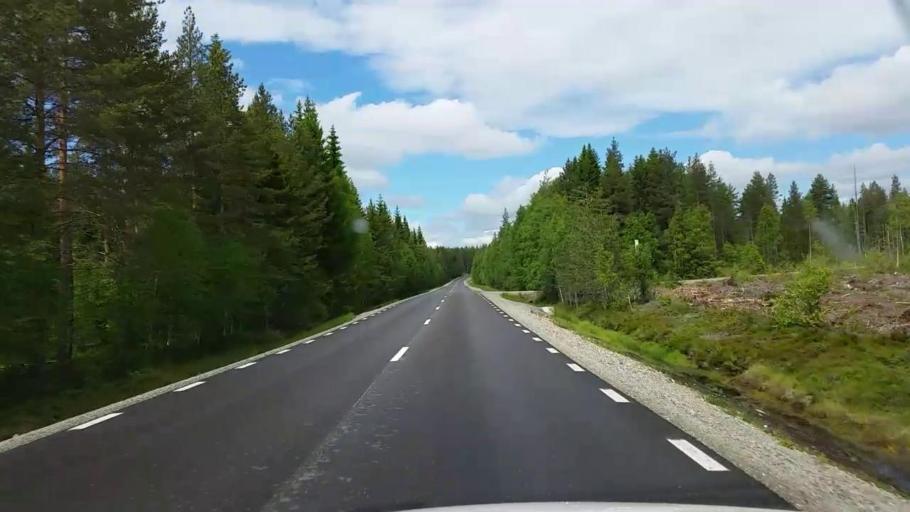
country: SE
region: Gaevleborg
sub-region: Sandvikens Kommun
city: Jarbo
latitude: 60.8927
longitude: 16.3792
